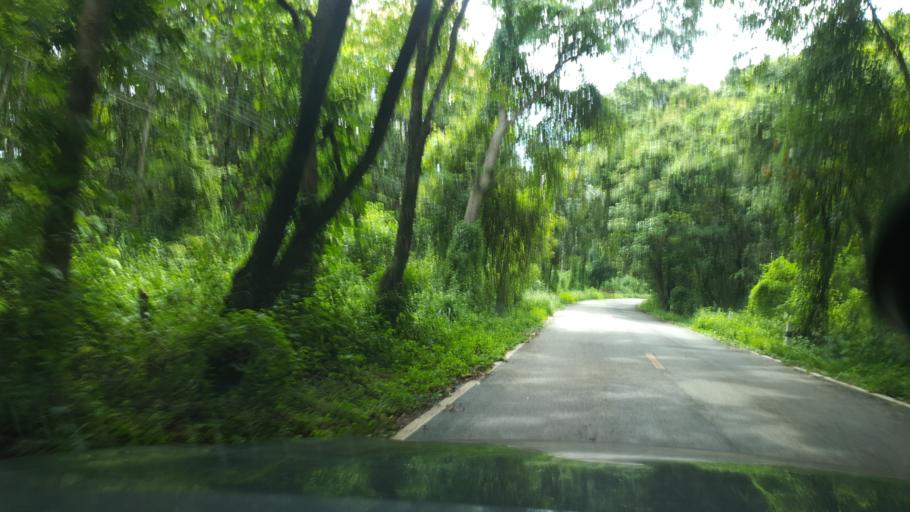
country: TH
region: Lamphun
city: Mae Tha
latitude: 18.5274
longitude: 99.2571
